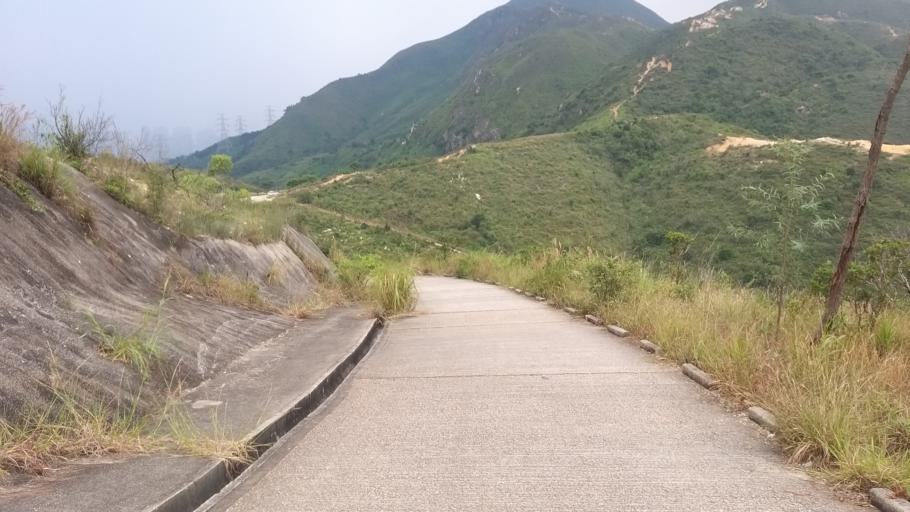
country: HK
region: Tuen Mun
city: Tuen Mun
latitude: 22.4089
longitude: 113.9520
